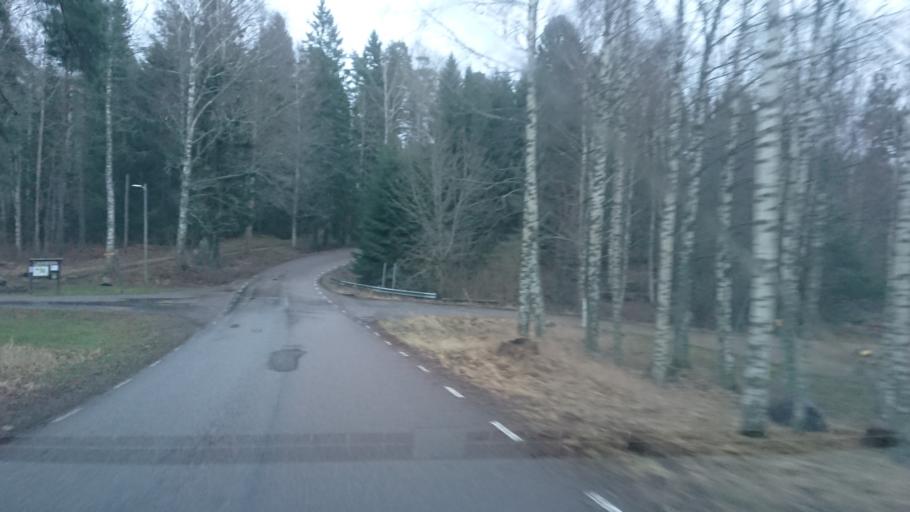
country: SE
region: Uppsala
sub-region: Osthammars Kommun
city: Bjorklinge
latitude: 60.0256
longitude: 17.5717
